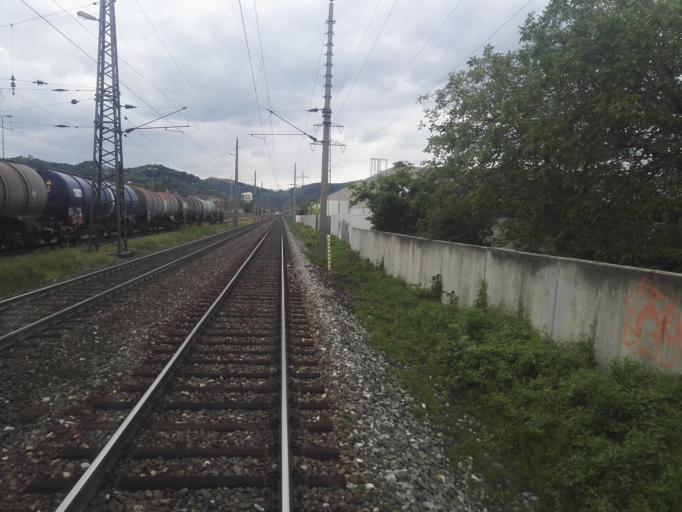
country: AT
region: Styria
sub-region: Graz Stadt
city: Goesting
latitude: 47.0887
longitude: 15.4076
